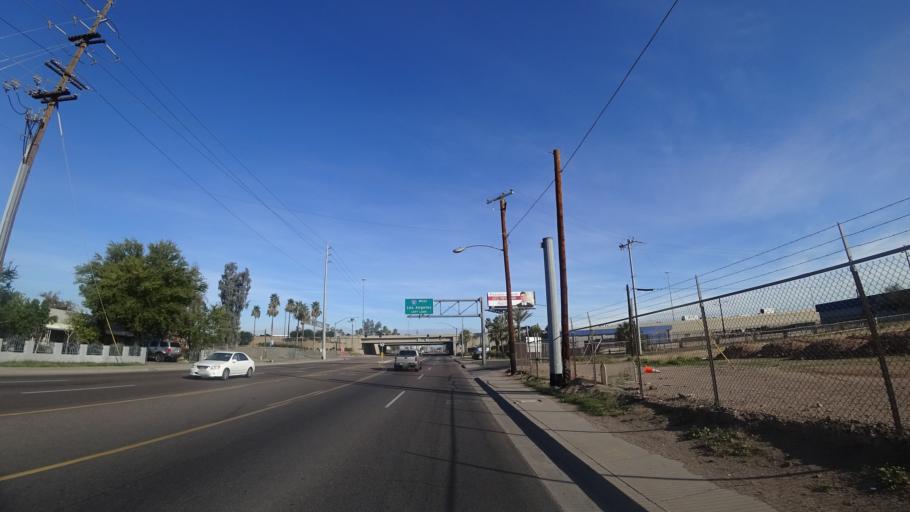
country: US
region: Arizona
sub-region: Maricopa County
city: Phoenix
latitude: 33.4602
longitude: -112.1172
